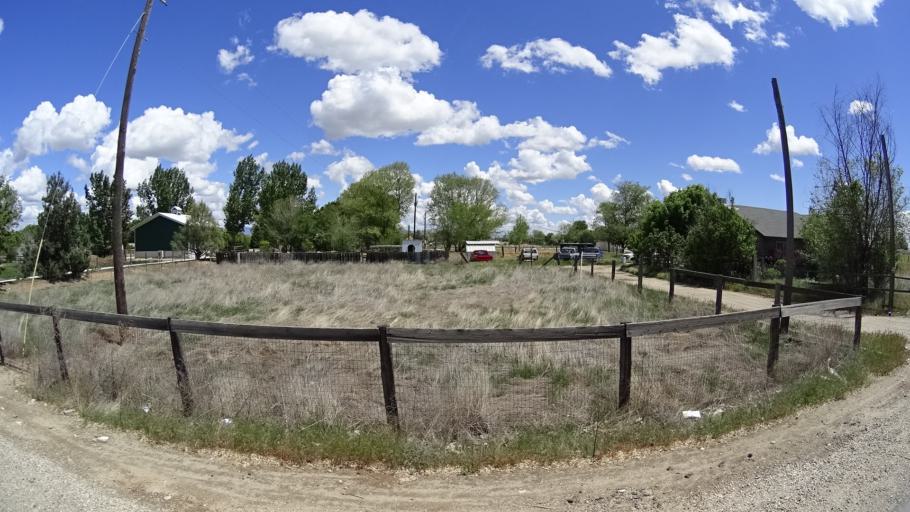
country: US
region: Idaho
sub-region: Ada County
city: Meridian
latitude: 43.5800
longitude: -116.4338
